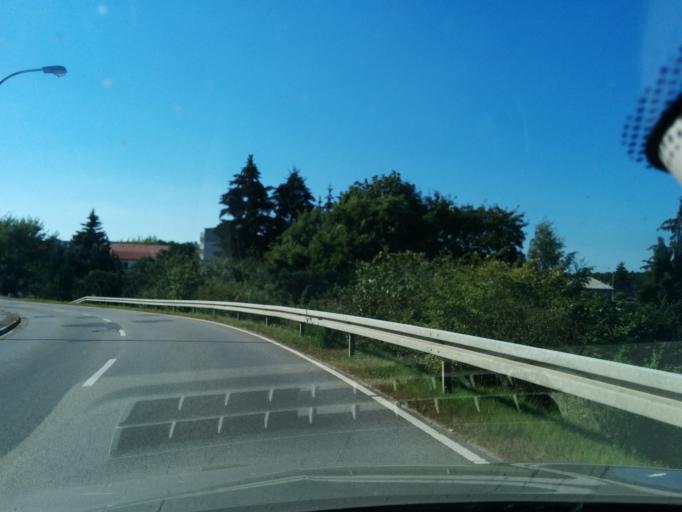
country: DE
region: Mecklenburg-Vorpommern
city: Torgelow
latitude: 53.6366
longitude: 14.0250
